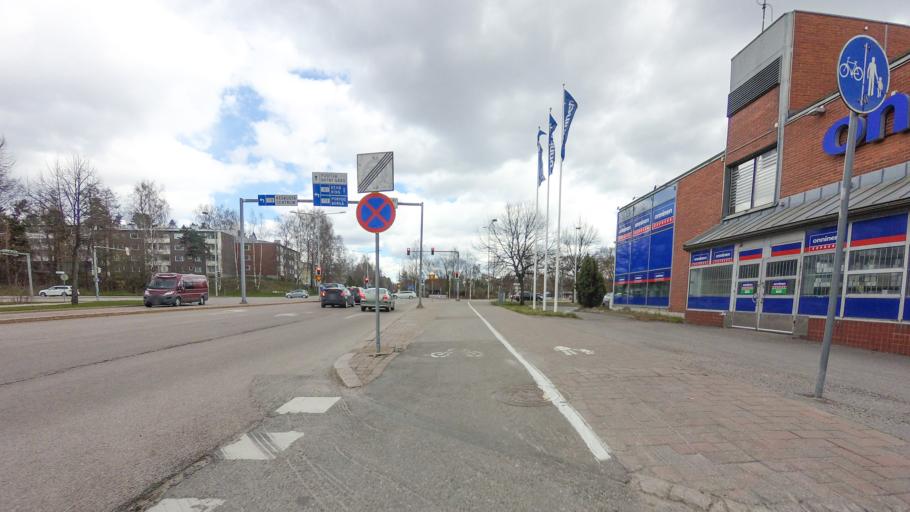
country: FI
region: Uusimaa
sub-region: Helsinki
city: Vantaa
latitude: 60.2098
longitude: 25.0900
